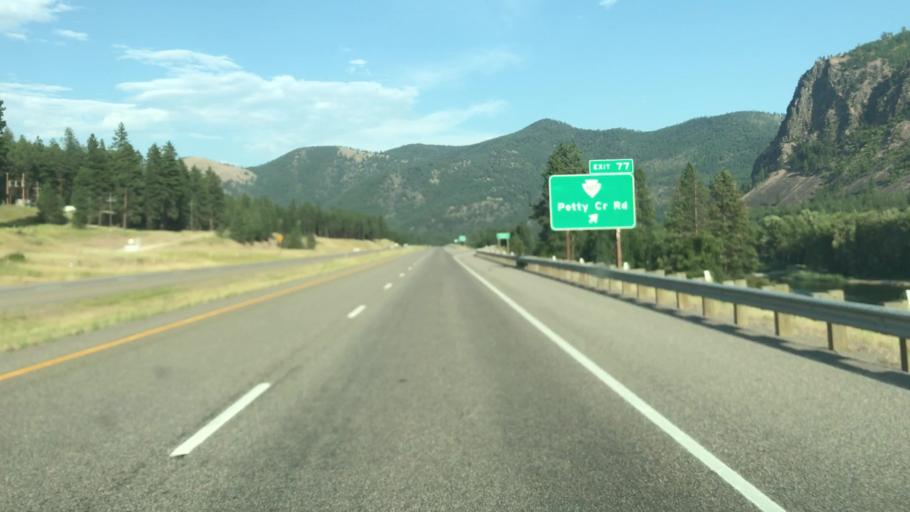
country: US
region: Montana
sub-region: Missoula County
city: Frenchtown
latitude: 46.9948
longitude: -114.4524
